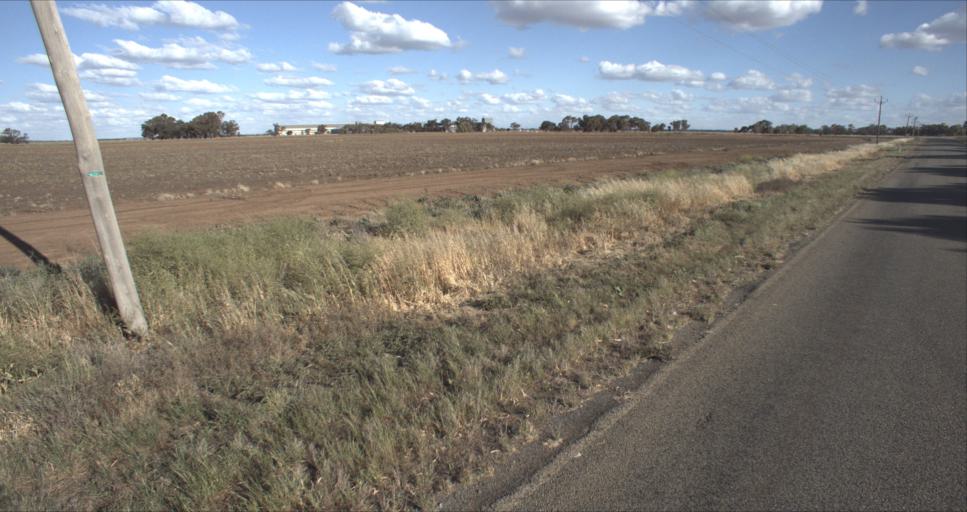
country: AU
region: New South Wales
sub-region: Leeton
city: Leeton
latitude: -34.5502
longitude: 146.2792
